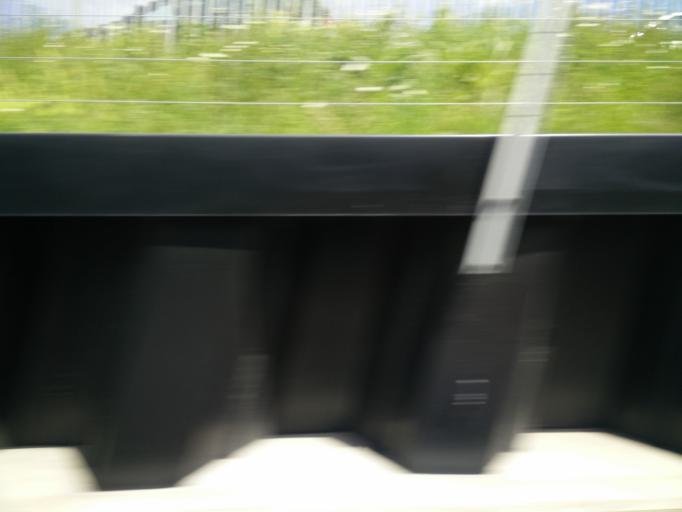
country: GB
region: England
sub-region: Luton
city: Luton
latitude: 51.8782
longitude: -0.4041
